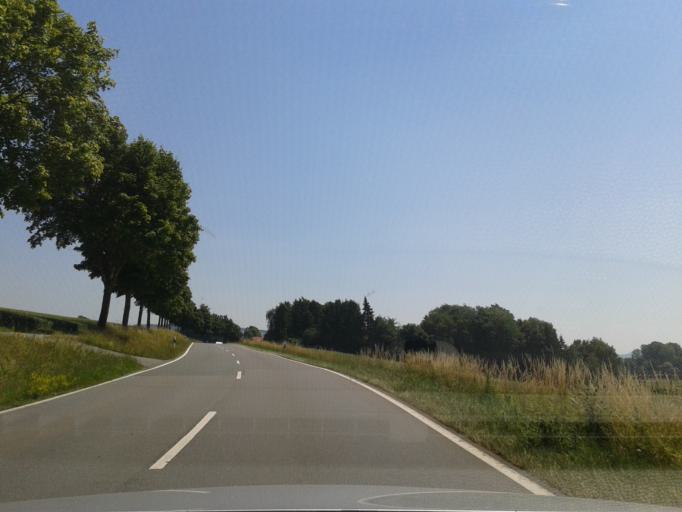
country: DE
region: North Rhine-Westphalia
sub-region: Regierungsbezirk Detmold
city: Dorentrup
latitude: 52.0310
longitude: 9.0188
